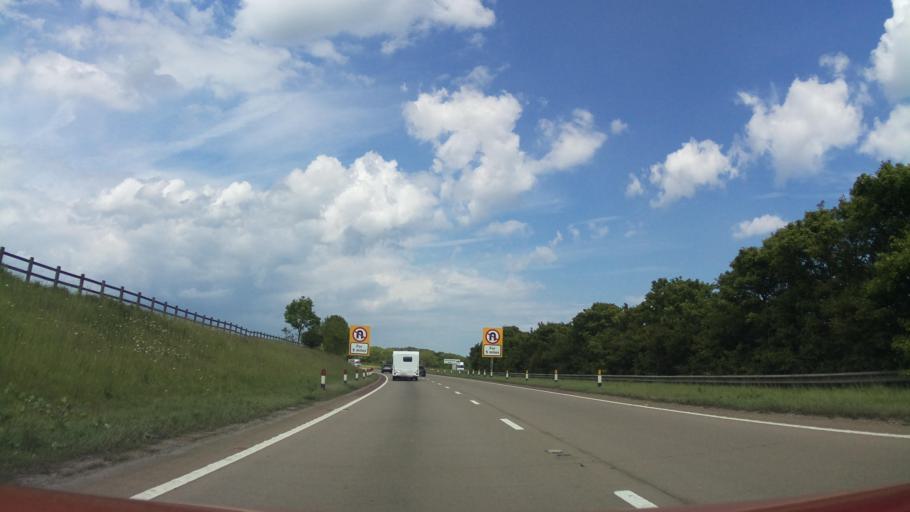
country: GB
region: England
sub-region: Stockton-on-Tees
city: Billingham
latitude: 54.6369
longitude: -1.3007
